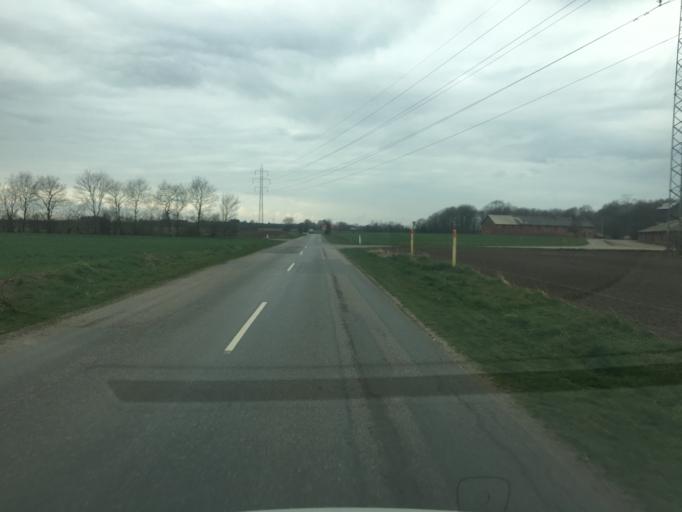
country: DK
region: South Denmark
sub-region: Aabenraa Kommune
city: Rodekro
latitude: 55.0383
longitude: 9.2178
